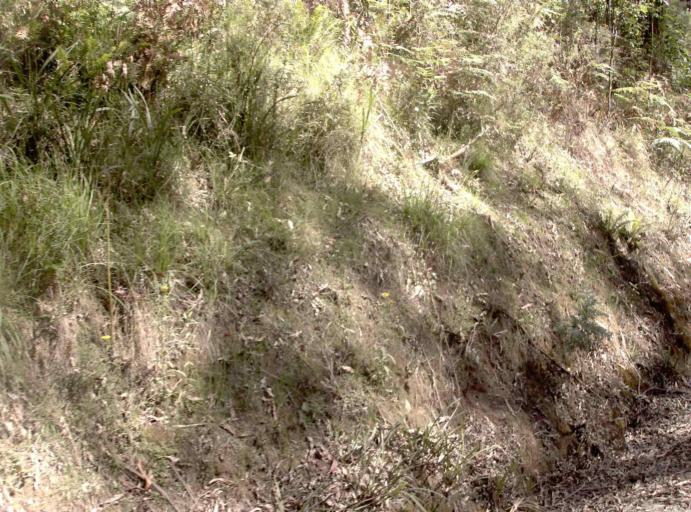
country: AU
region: New South Wales
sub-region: Bombala
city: Bombala
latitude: -37.2231
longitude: 148.7483
